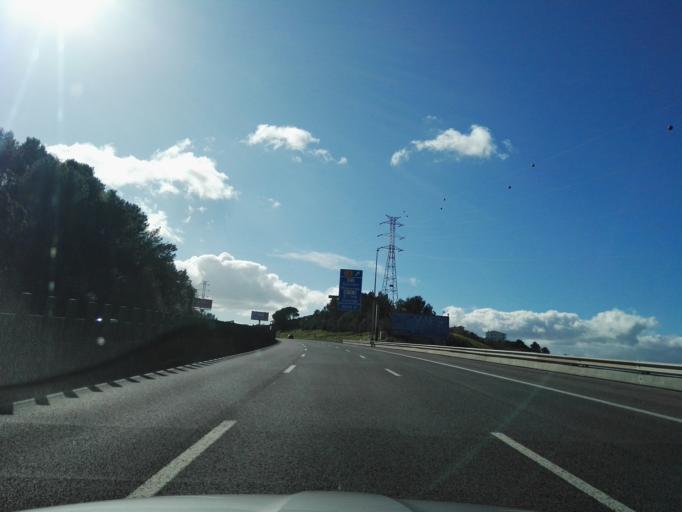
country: PT
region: Lisbon
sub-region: Vila Franca de Xira
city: Vialonga
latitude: 38.8665
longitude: -9.0776
